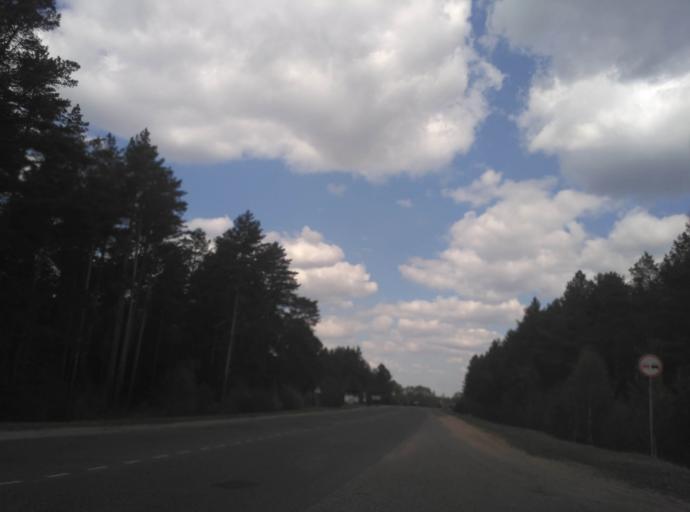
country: BY
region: Minsk
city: Il'ya
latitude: 54.3180
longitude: 27.2473
